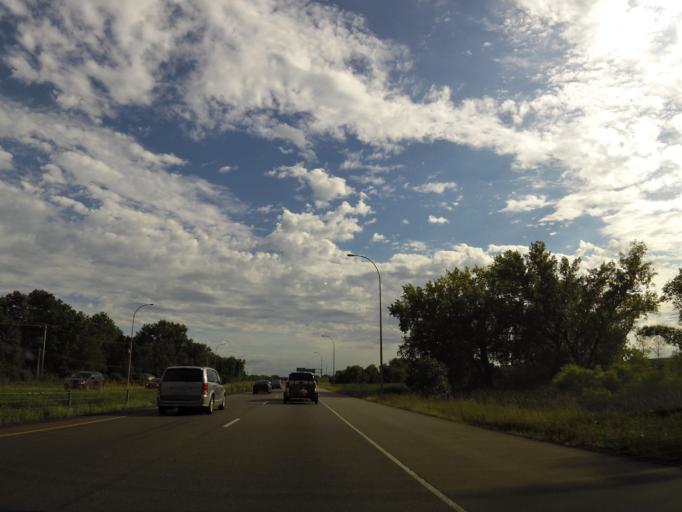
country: US
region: Minnesota
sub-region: Hennepin County
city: New Hope
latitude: 45.0642
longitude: -93.4010
